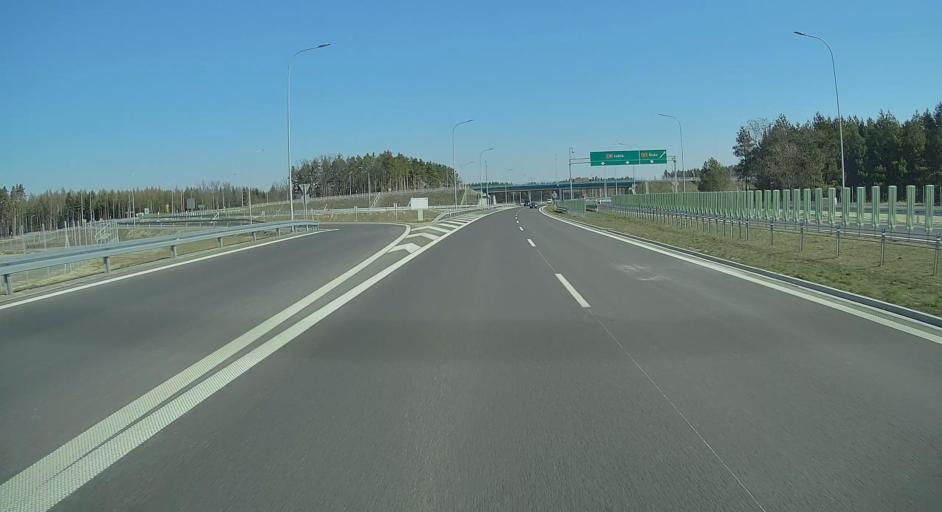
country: PL
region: Subcarpathian Voivodeship
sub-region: Powiat nizanski
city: Konczyce
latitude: 50.4705
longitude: 22.1493
